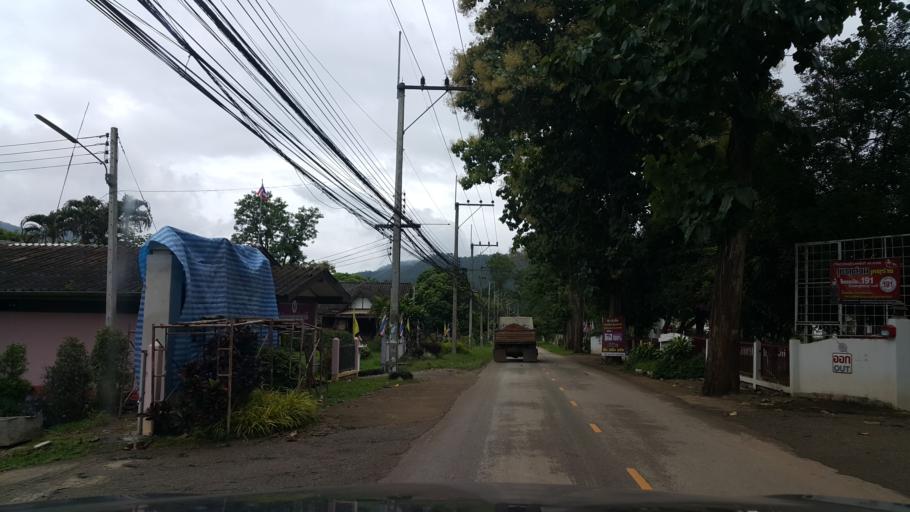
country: TH
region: Chiang Mai
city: Samoeng
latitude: 18.8490
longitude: 98.7320
